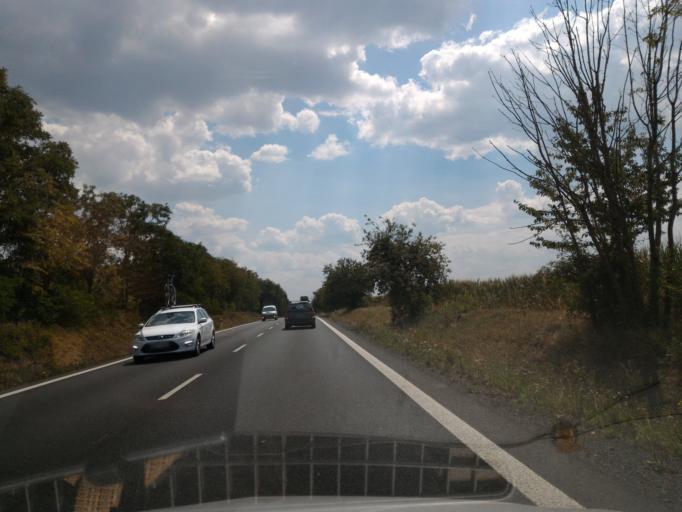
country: CZ
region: Central Bohemia
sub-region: Okres Kutna Hora
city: Caslav
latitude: 49.8741
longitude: 15.4325
